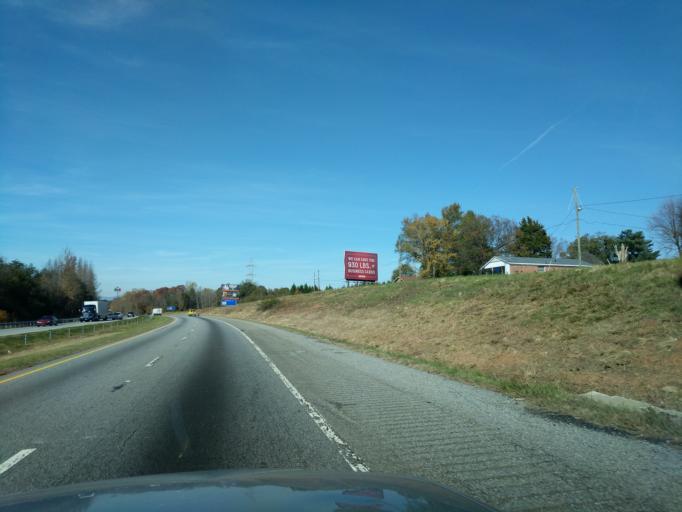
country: US
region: South Carolina
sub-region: Spartanburg County
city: Southern Shops
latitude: 34.9991
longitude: -82.0205
